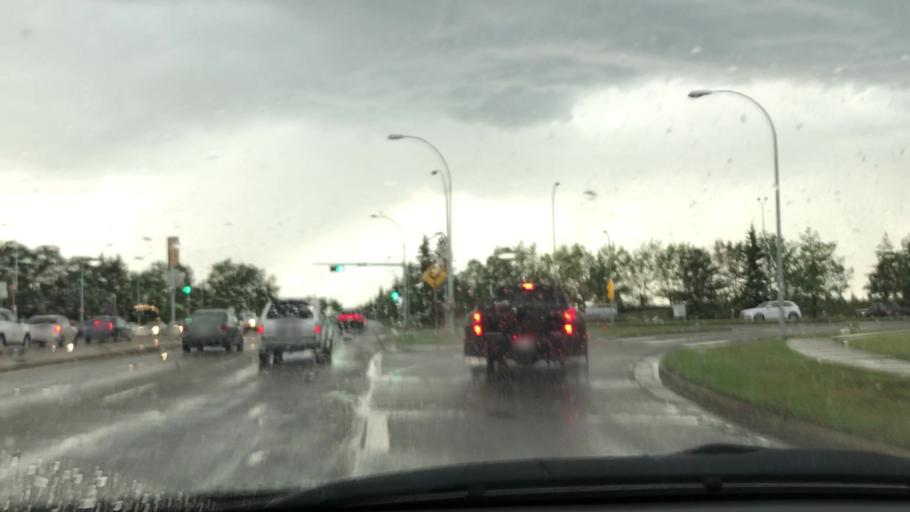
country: CA
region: Alberta
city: Edmonton
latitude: 53.4537
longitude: -113.4338
